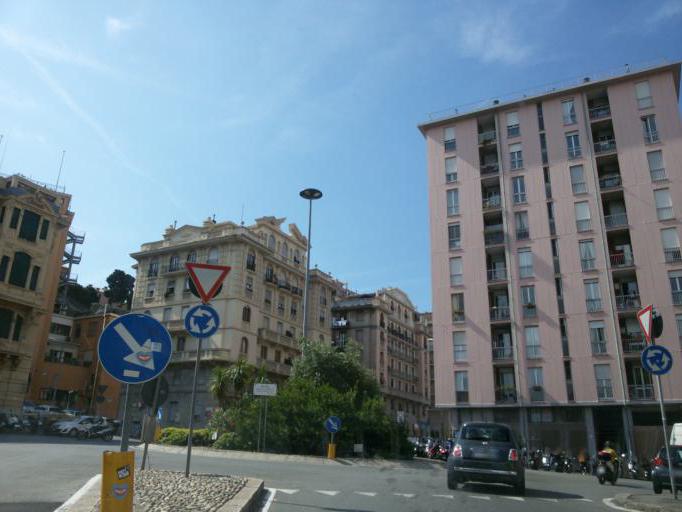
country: IT
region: Liguria
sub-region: Provincia di Genova
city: San Teodoro
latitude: 44.4013
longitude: 8.9540
